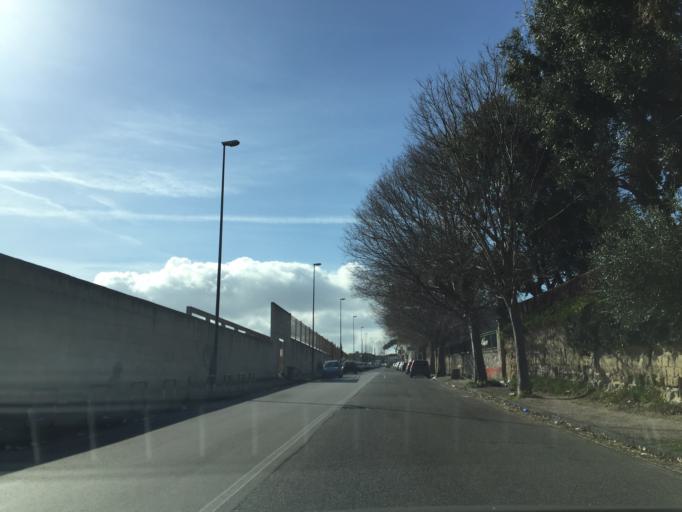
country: IT
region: Campania
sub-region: Provincia di Napoli
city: Casavatore
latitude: 40.8697
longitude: 14.2891
